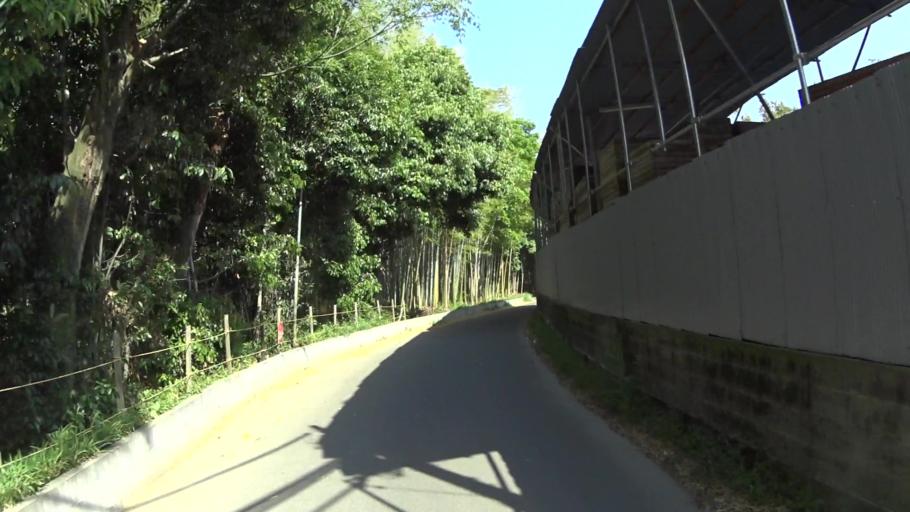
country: JP
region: Kyoto
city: Muko
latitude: 34.9440
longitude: 135.6807
